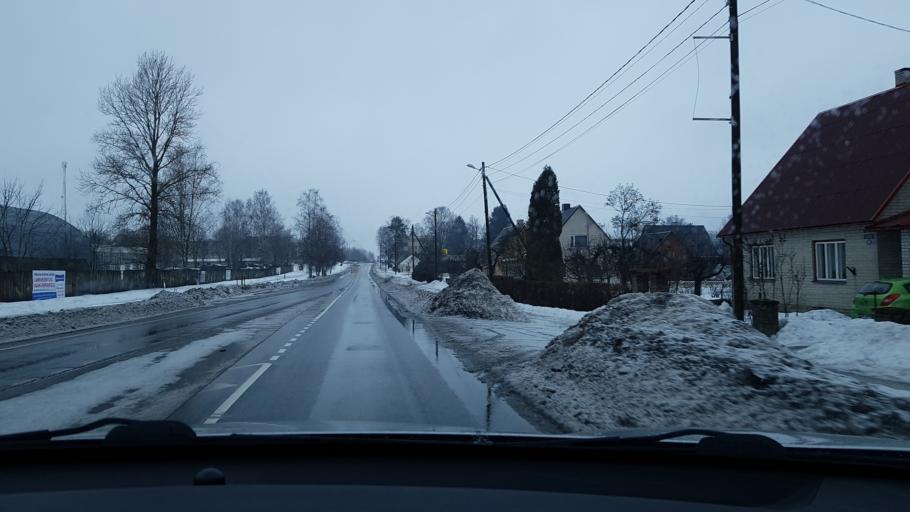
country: EE
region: Jaervamaa
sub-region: Tueri vald
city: Tueri
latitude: 58.8113
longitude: 25.4104
